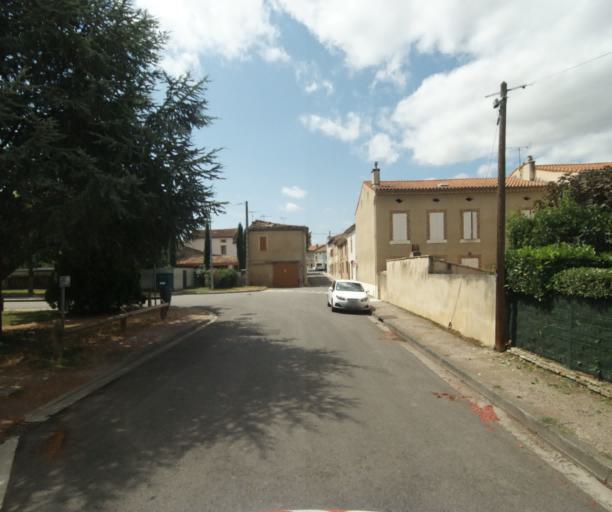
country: FR
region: Midi-Pyrenees
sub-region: Departement de la Haute-Garonne
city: Revel
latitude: 43.4595
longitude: 2.0076
